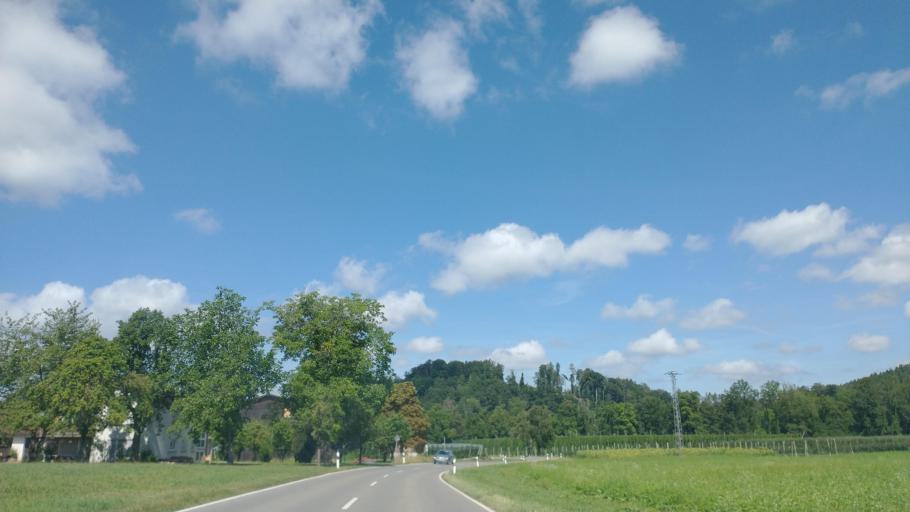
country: DE
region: Baden-Wuerttemberg
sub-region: Tuebingen Region
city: Kressbronn am Bodensee
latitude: 47.6272
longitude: 9.6025
